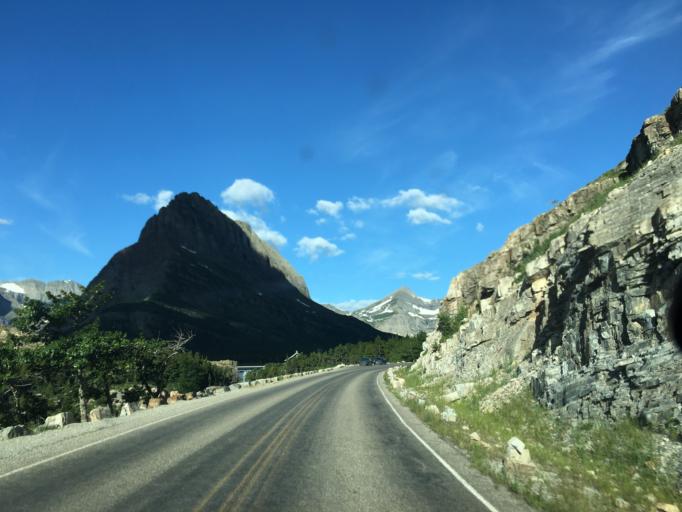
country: CA
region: Alberta
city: Cardston
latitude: 48.8011
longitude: -113.6526
